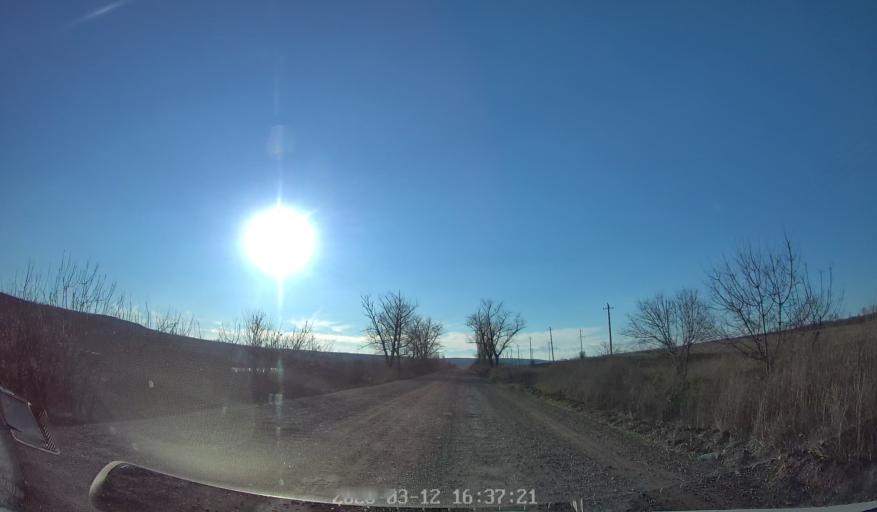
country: MD
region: Anenii Noi
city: Anenii Noi
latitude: 46.8154
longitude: 29.1890
